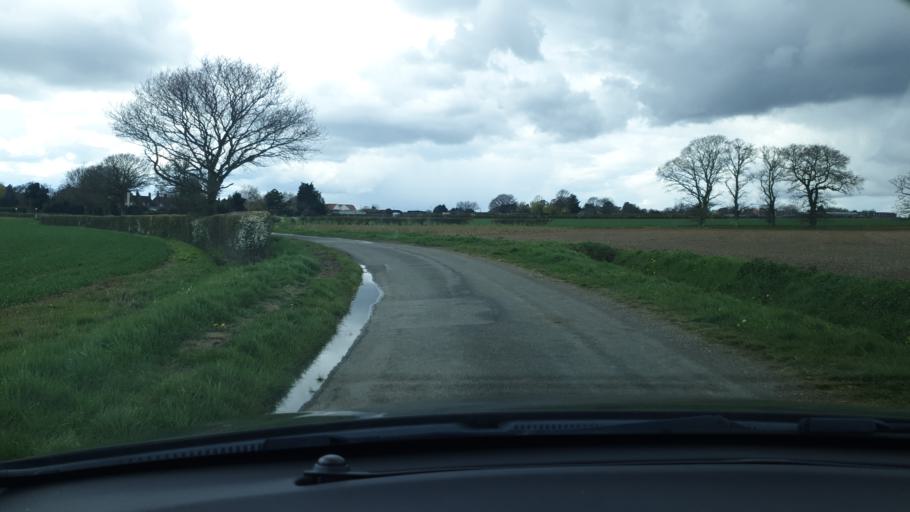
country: GB
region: England
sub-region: Essex
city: Mistley
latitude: 51.8931
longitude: 1.1140
